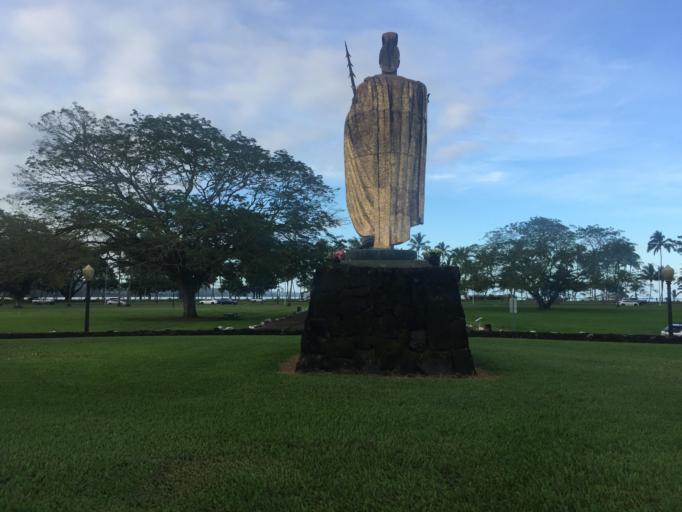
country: US
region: Hawaii
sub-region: Hawaii County
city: Hilo
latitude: 19.7208
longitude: -155.0769
